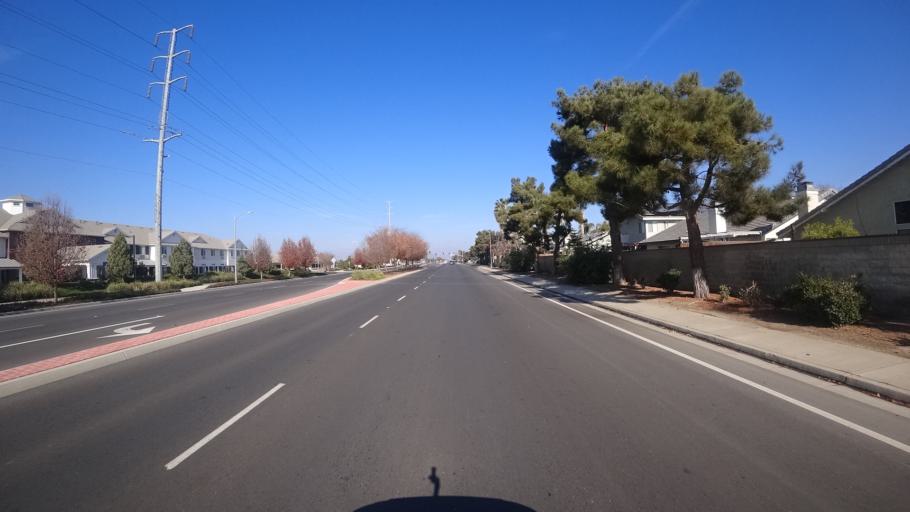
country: US
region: California
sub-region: Kern County
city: Greenacres
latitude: 35.3157
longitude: -119.1280
